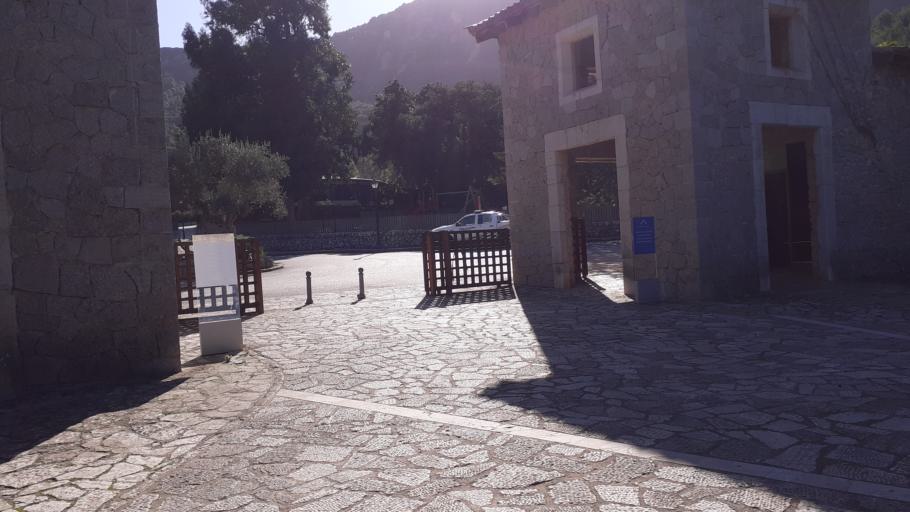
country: ES
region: Balearic Islands
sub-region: Illes Balears
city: Escorca
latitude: 39.8222
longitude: 2.8840
